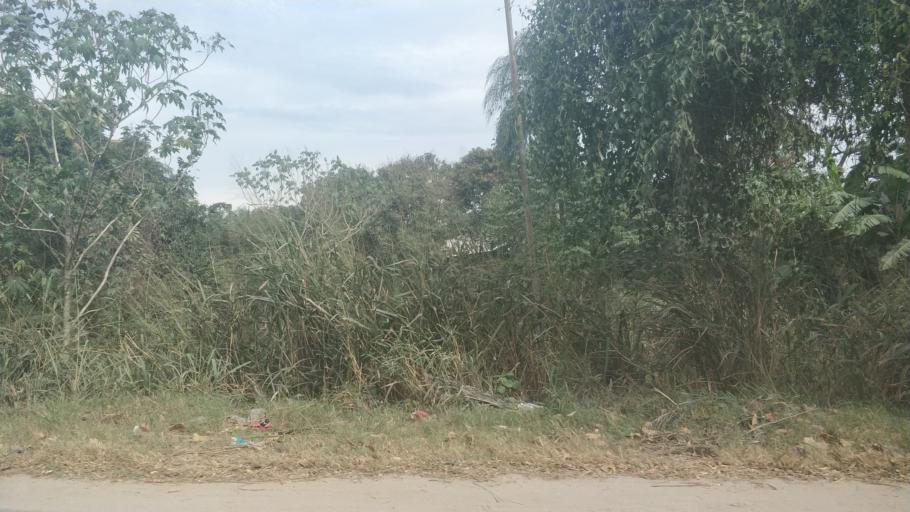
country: BR
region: Rio de Janeiro
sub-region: Seropedica
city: Seropedica
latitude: -22.8101
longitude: -43.6325
